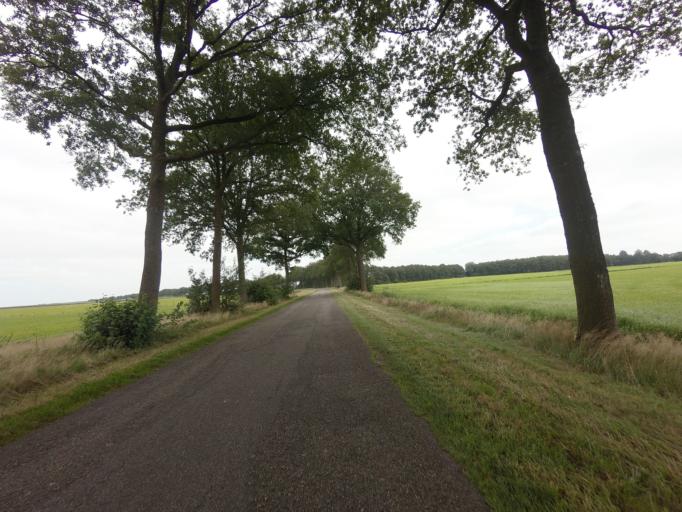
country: NL
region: Drenthe
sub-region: Gemeente Westerveld
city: Dwingeloo
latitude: 52.9671
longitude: 6.3530
